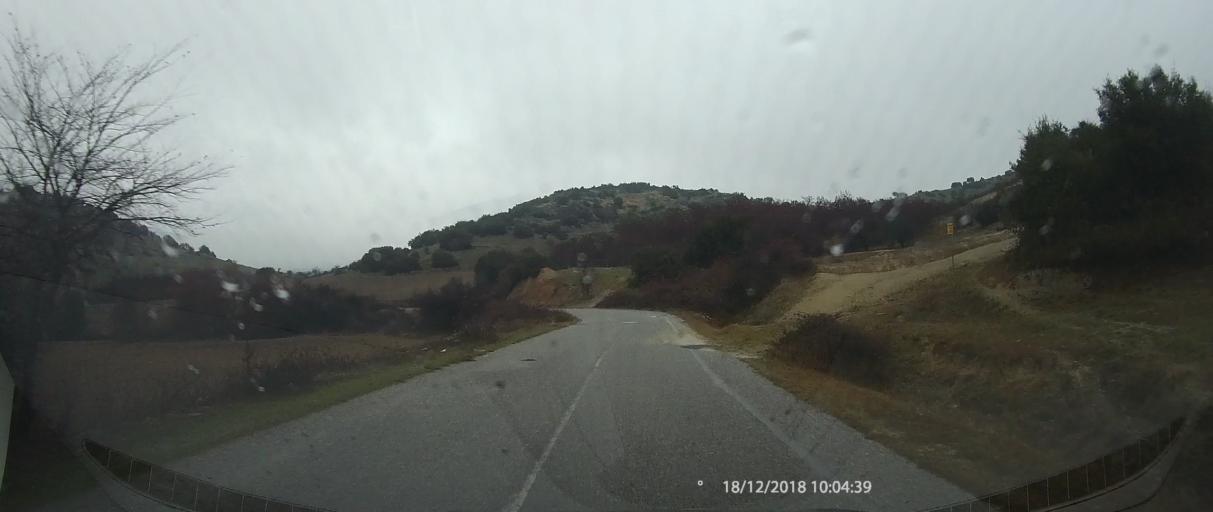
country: GR
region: Thessaly
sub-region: Nomos Larisis
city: Livadi
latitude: 40.0546
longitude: 22.2223
